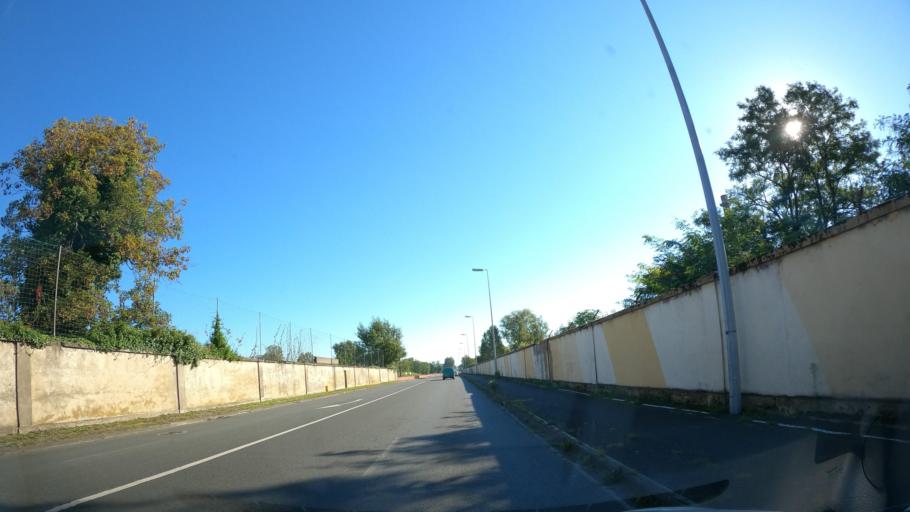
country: FR
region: Aquitaine
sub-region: Departement de la Dordogne
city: Bergerac
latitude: 44.8460
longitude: 0.5145
